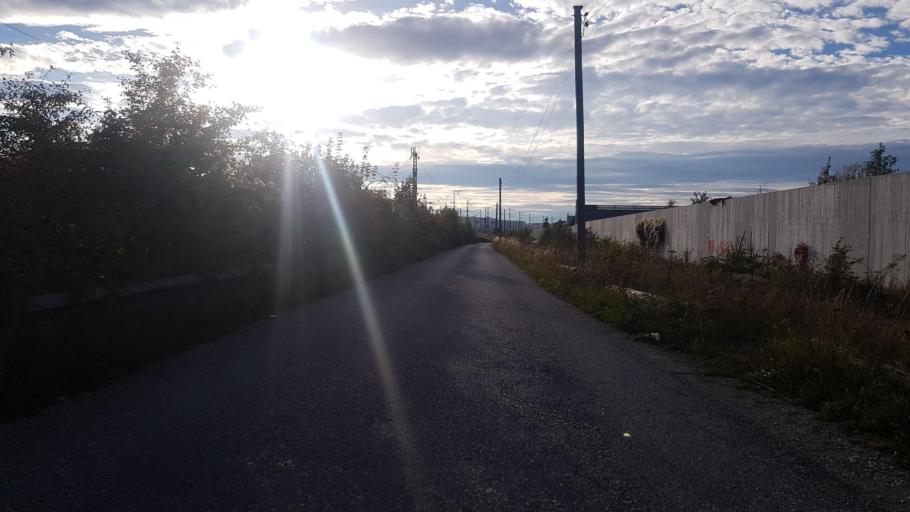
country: DE
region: Bavaria
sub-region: Upper Bavaria
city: Pasing
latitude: 48.1481
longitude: 11.4791
